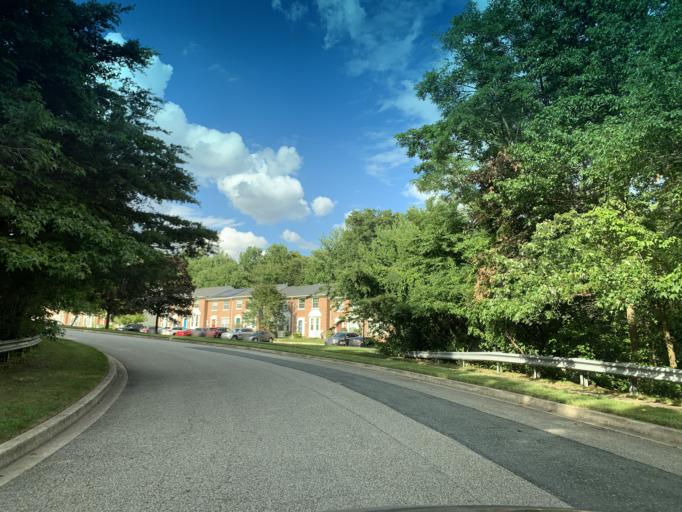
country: US
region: Maryland
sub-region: Harford County
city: Riverside
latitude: 39.4820
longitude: -76.2419
